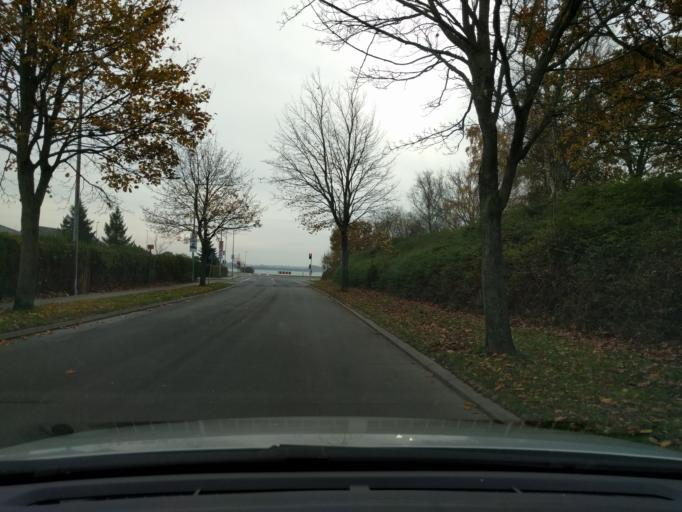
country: DK
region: South Denmark
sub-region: Kerteminde Kommune
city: Kerteminde
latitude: 55.4543
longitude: 10.6386
